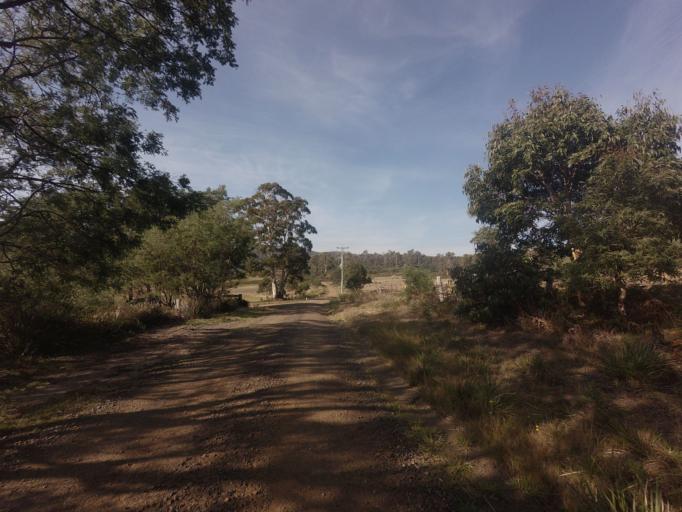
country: AU
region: Tasmania
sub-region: Sorell
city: Sorell
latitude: -42.5315
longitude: 147.4399
